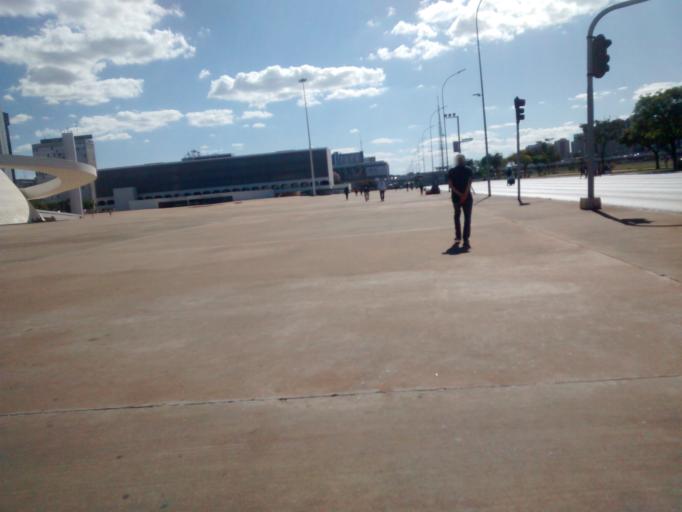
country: BR
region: Federal District
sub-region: Brasilia
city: Brasilia
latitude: -15.7969
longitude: -47.8771
